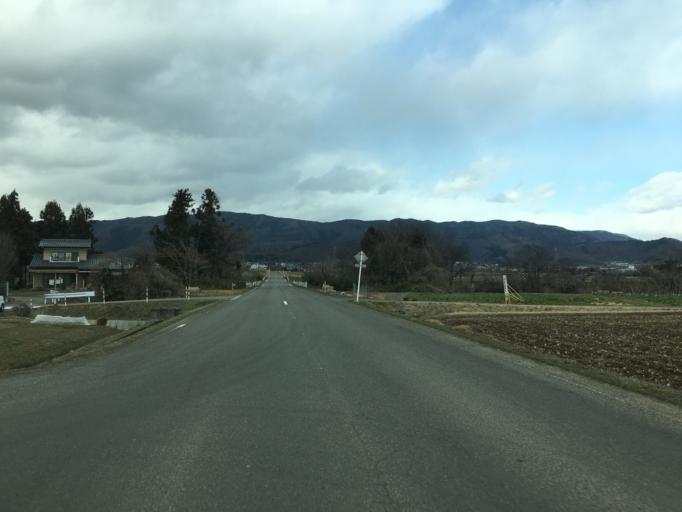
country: JP
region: Fukushima
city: Hobaramachi
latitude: 37.8610
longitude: 140.5380
